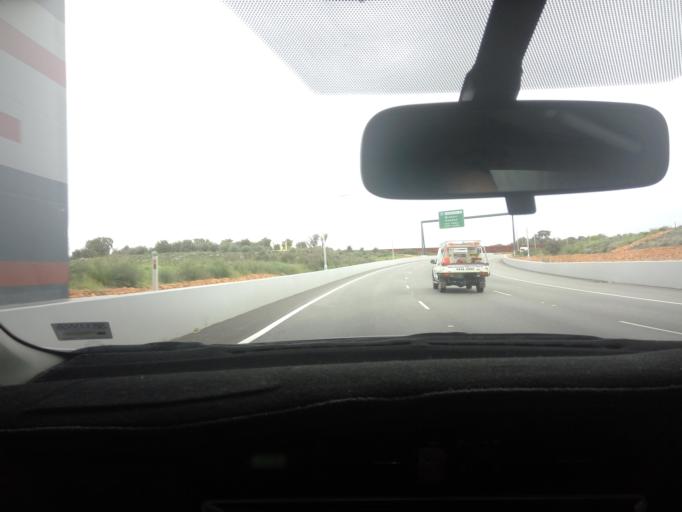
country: AU
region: Western Australia
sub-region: Belmont
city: Kewdale
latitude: -31.9634
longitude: 115.9560
